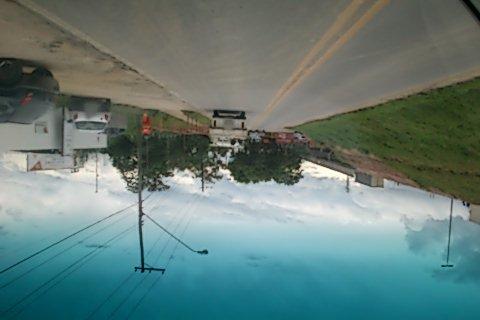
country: BR
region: Sao Paulo
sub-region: Jacarei
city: Jacarei
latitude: -23.2767
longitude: -45.9774
